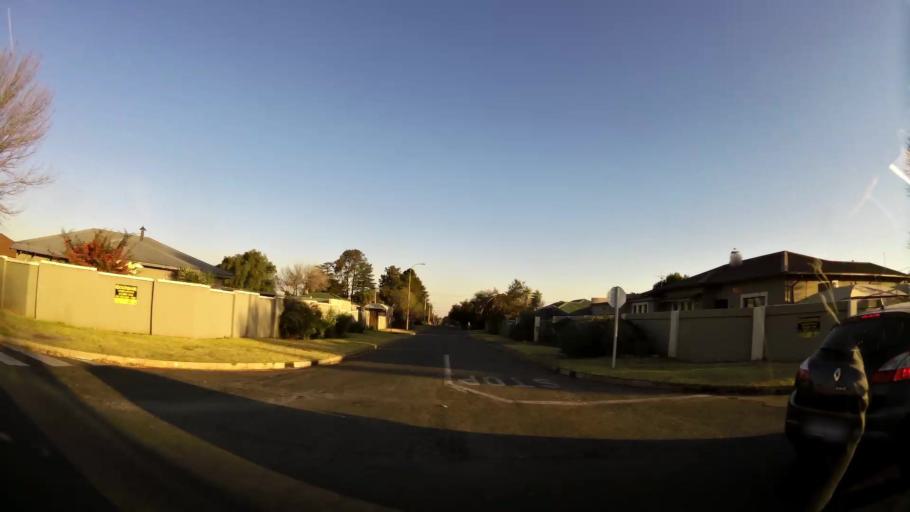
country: ZA
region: Gauteng
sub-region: City of Johannesburg Metropolitan Municipality
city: Roodepoort
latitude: -26.1584
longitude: 27.8913
